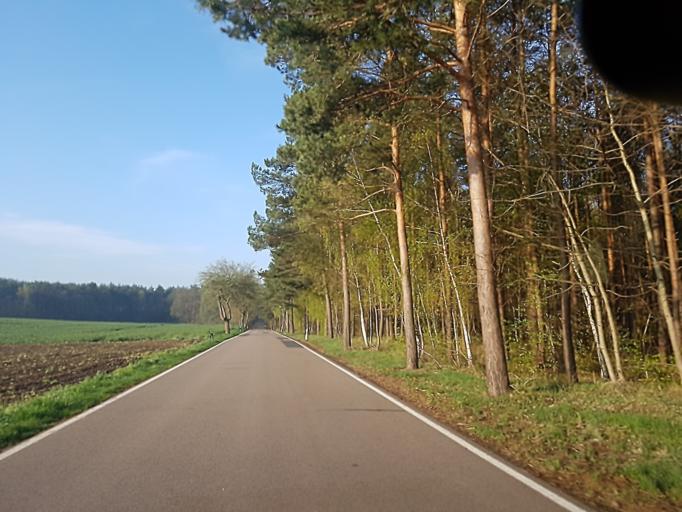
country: DE
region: Saxony
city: Cavertitz
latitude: 51.4207
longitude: 13.1512
